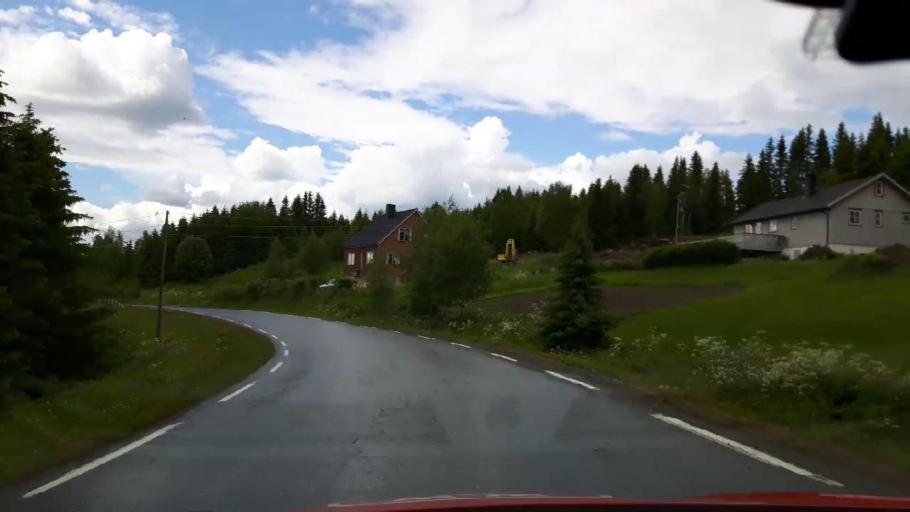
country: NO
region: Nord-Trondelag
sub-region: Lierne
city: Sandvika
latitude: 64.1096
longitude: 13.9804
